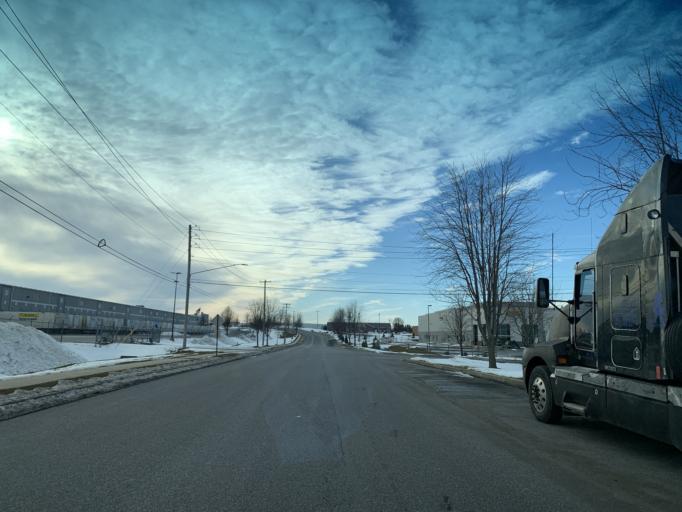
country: US
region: Pennsylvania
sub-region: Cumberland County
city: Carlisle
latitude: 40.1900
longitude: -77.2345
